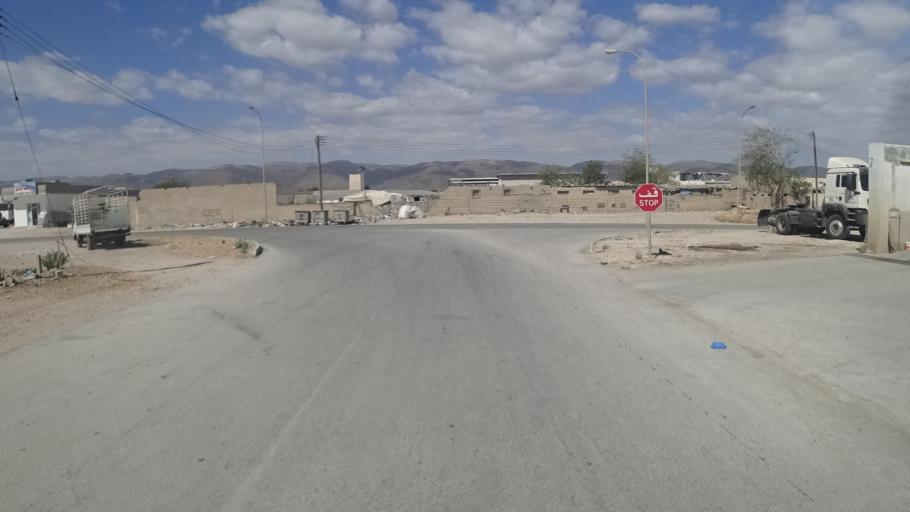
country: OM
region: Zufar
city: Salalah
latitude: 17.0251
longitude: 54.0354
